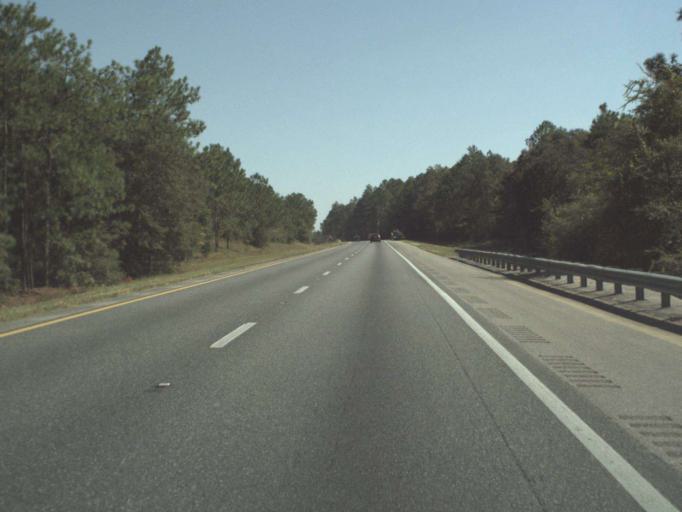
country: US
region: Florida
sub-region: Okaloosa County
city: Crestview
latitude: 30.7139
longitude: -86.6310
